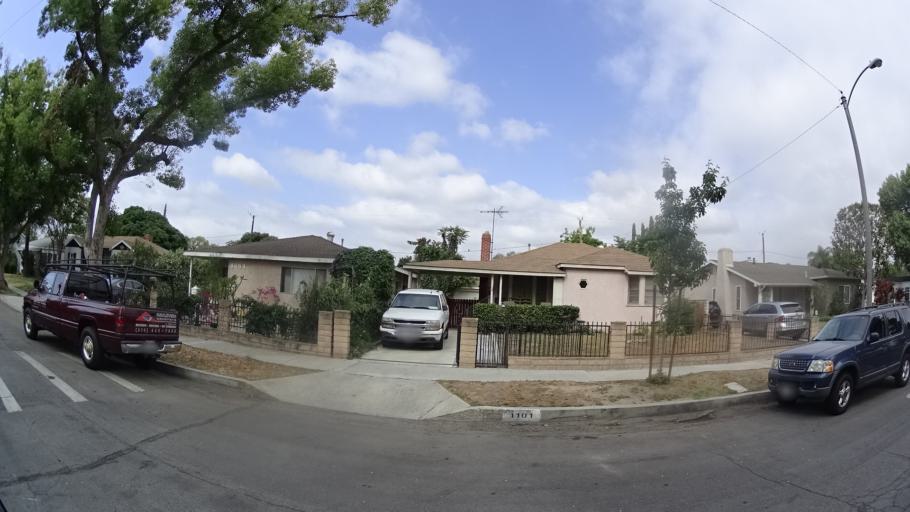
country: US
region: California
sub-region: Los Angeles County
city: North Hollywood
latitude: 34.1679
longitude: -118.3529
